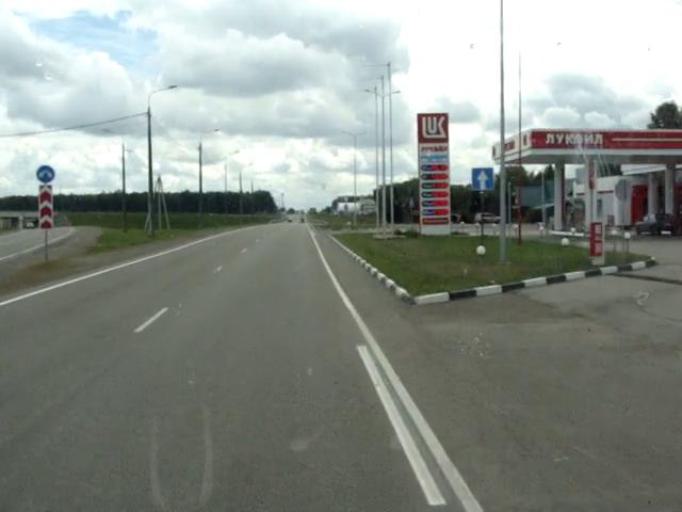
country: RU
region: Altai Krai
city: Zarya
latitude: 52.5800
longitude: 85.1762
